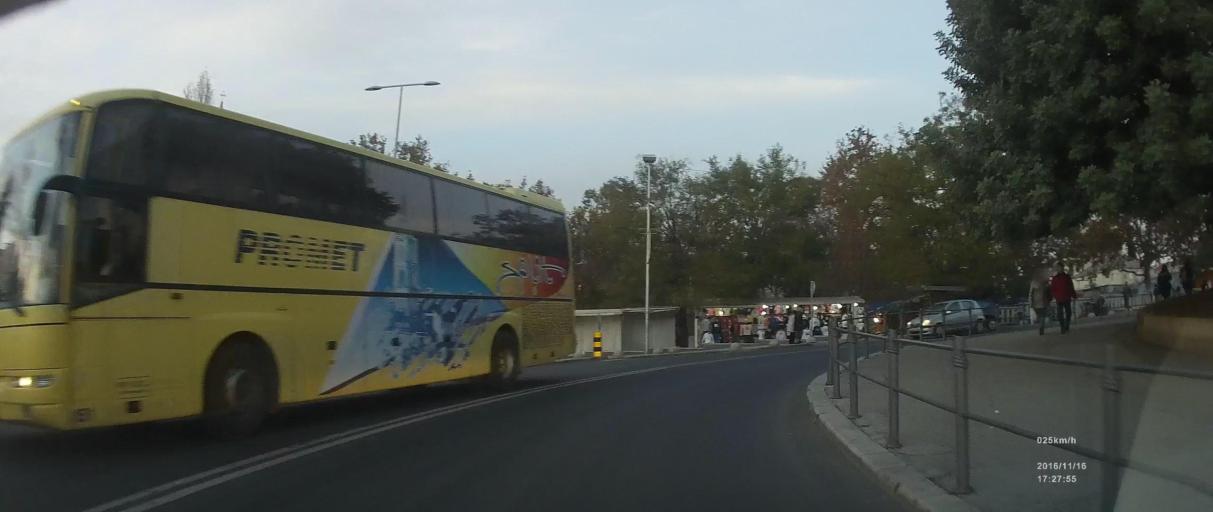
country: HR
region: Splitsko-Dalmatinska
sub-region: Grad Split
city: Split
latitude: 43.5067
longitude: 16.4412
